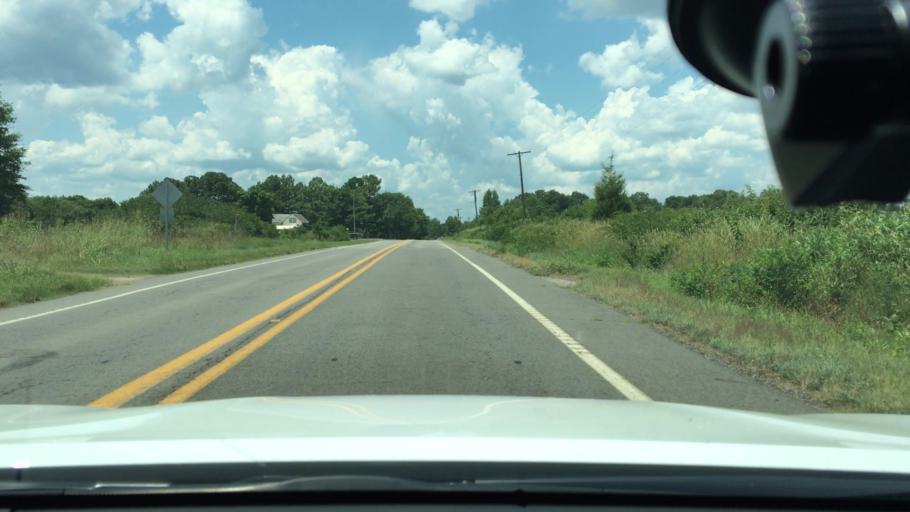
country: US
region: Arkansas
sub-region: Logan County
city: Booneville
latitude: 35.1477
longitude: -93.8376
